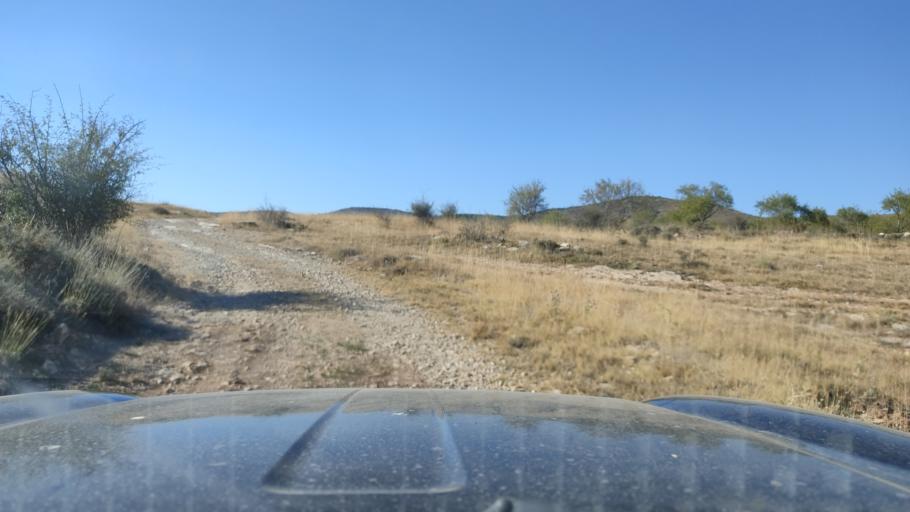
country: ES
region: Aragon
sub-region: Provincia de Teruel
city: Monforte de Moyuela
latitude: 41.0332
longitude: -1.0140
